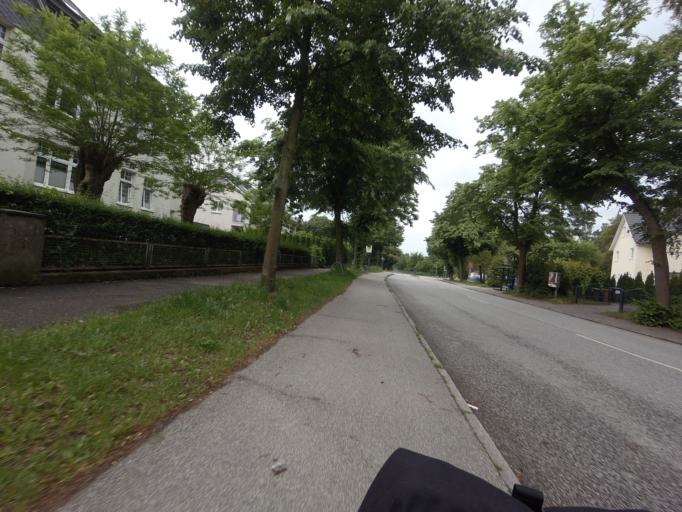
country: DE
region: Mecklenburg-Vorpommern
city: Selmsdorf
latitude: 53.9032
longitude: 10.8028
